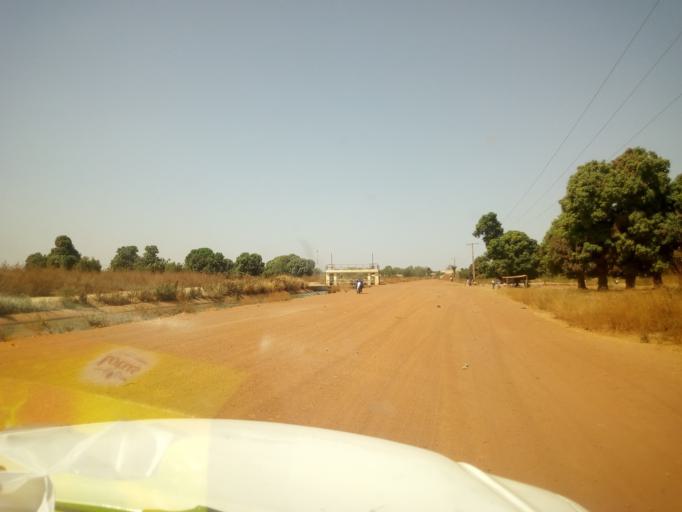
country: ML
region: Bamako
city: Bamako
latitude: 12.6203
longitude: -7.7707
